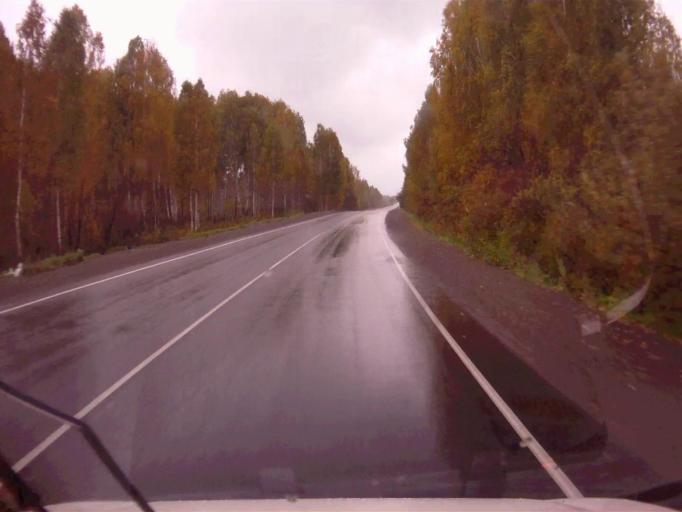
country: RU
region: Chelyabinsk
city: Argayash
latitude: 55.4788
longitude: 60.7611
